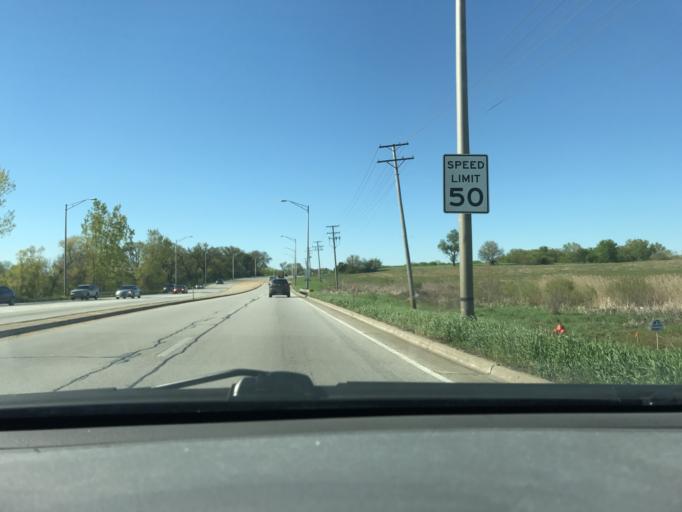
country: US
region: Illinois
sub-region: Kane County
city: Sleepy Hollow
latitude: 42.0647
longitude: -88.3358
